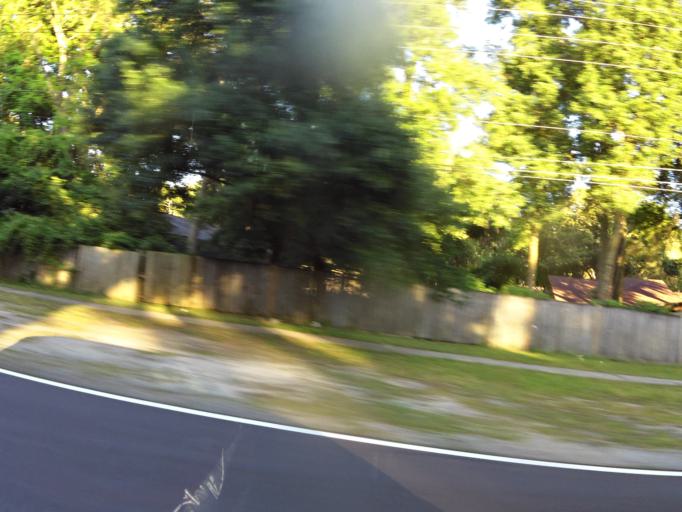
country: US
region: Florida
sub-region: Duval County
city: Atlantic Beach
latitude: 30.3782
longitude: -81.5104
